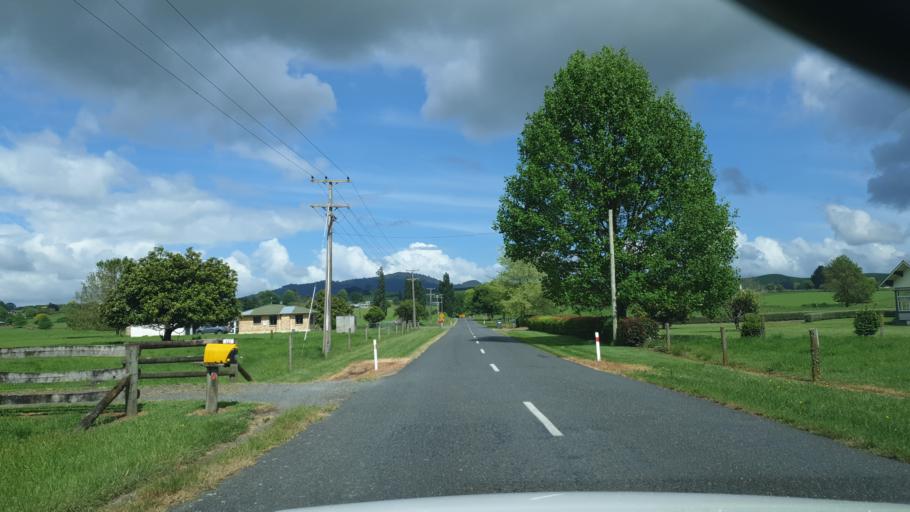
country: NZ
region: Waikato
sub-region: Matamata-Piako District
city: Matamata
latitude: -37.8262
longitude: 175.7362
